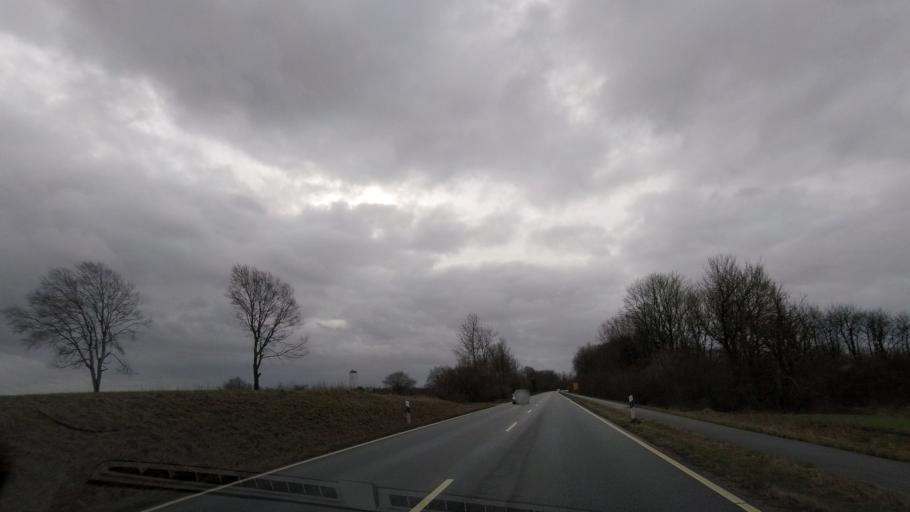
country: DE
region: Schleswig-Holstein
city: Schaalby
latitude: 54.5597
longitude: 9.6284
